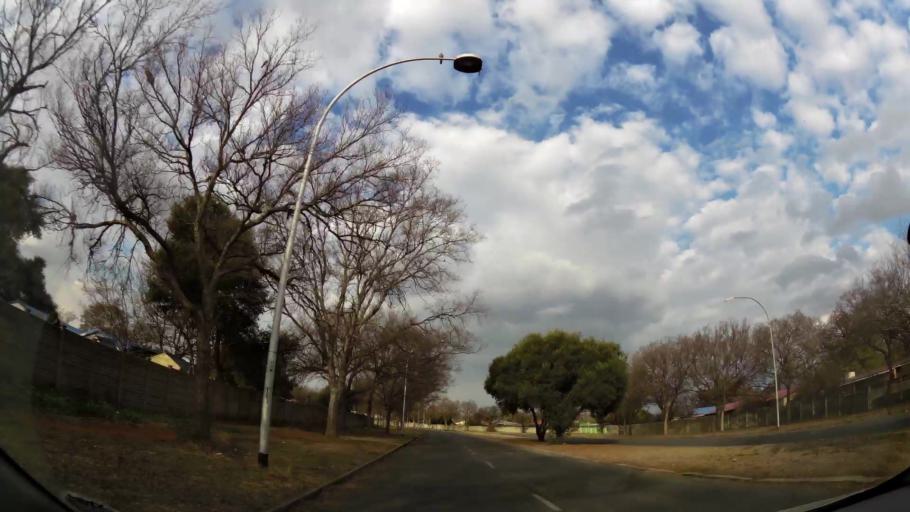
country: ZA
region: Orange Free State
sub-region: Fezile Dabi District Municipality
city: Sasolburg
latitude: -26.8180
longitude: 27.8124
